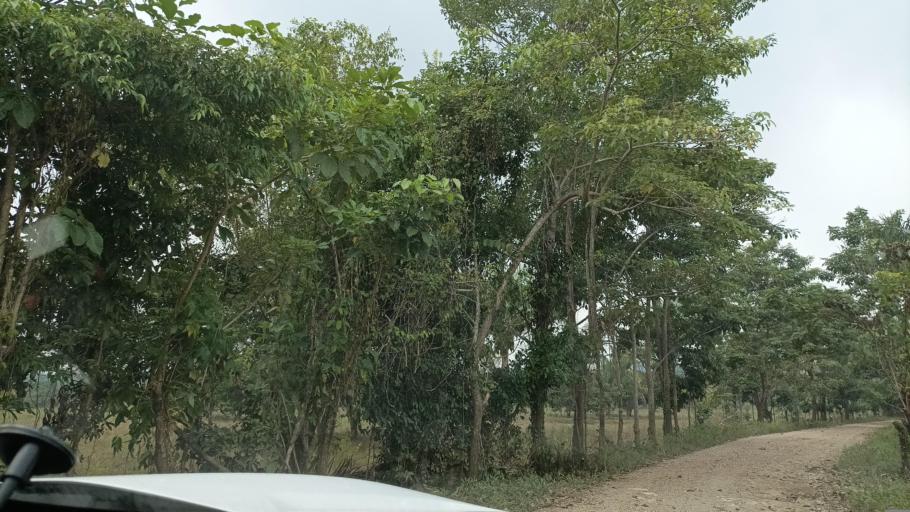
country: MX
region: Veracruz
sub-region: Uxpanapa
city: Poblado 10
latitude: 17.5678
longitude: -94.2268
